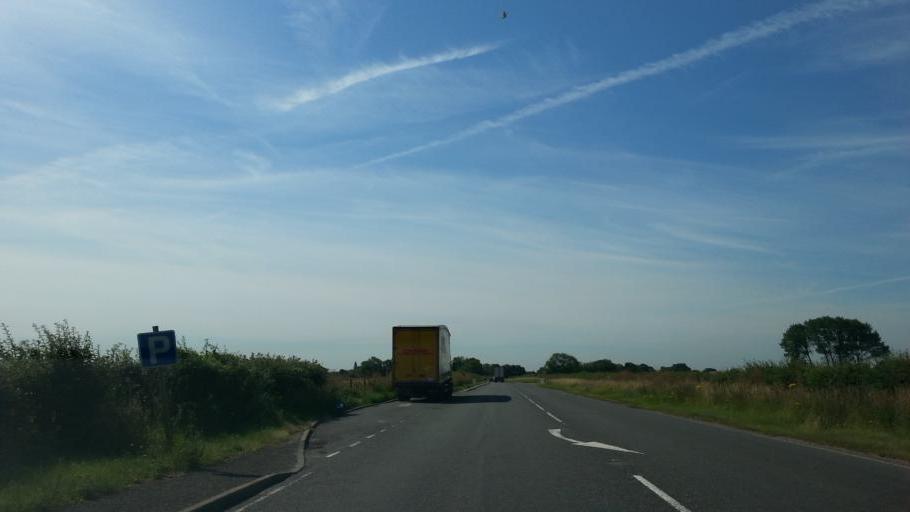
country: GB
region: England
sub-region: Nottinghamshire
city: Newark on Trent
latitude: 53.1143
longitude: -0.8205
